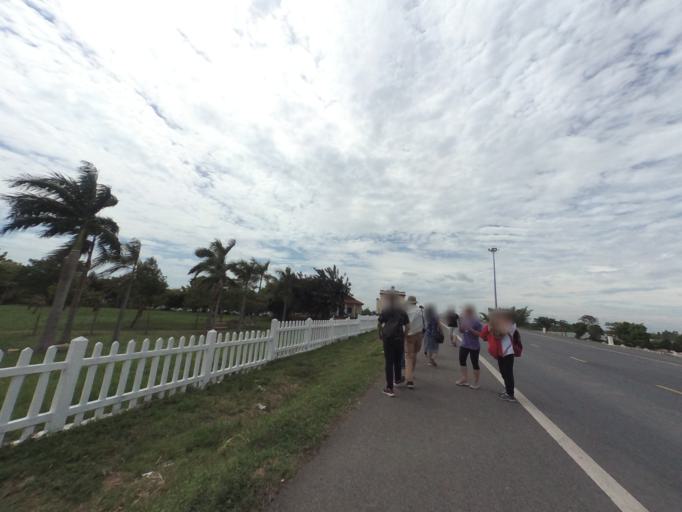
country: VN
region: Quang Tri
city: Ho Xa
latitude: 17.0058
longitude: 107.0508
